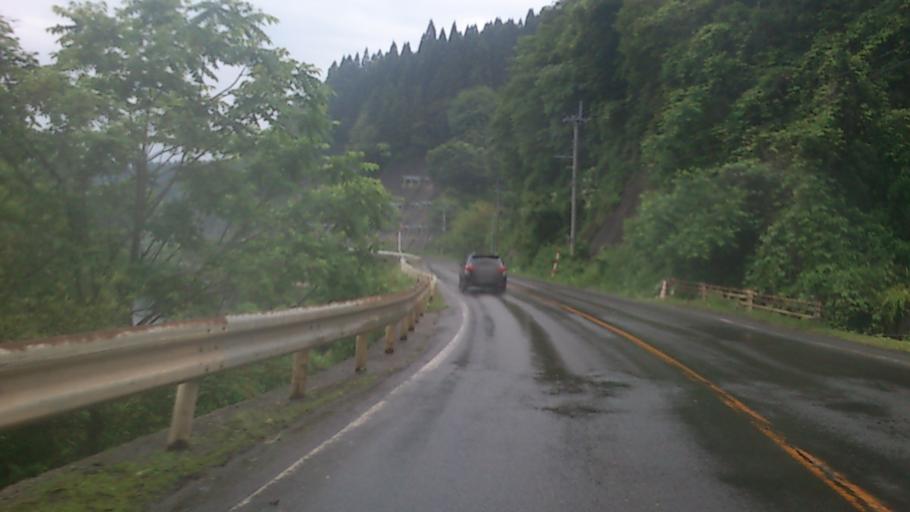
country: JP
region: Akita
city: Takanosu
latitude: 40.2398
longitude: 140.2438
